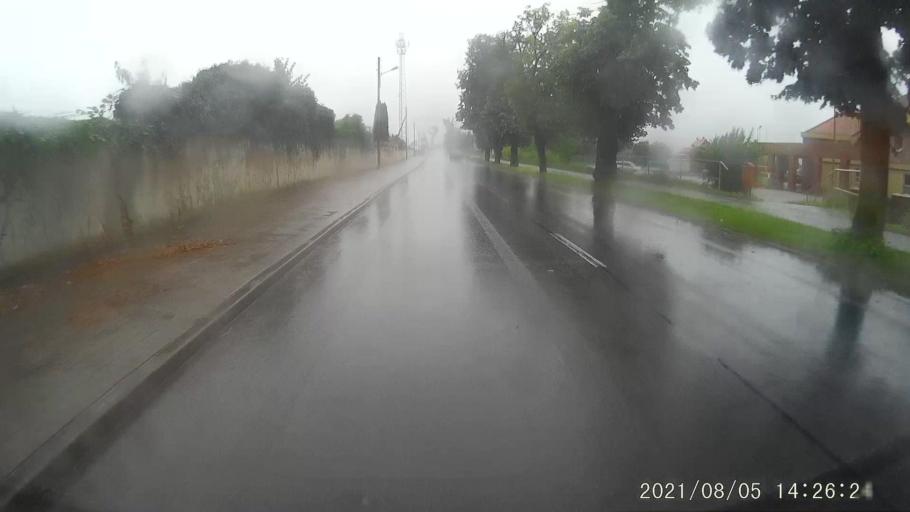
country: PL
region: Opole Voivodeship
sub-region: Powiat nyski
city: Korfantow
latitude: 50.4881
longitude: 17.6016
